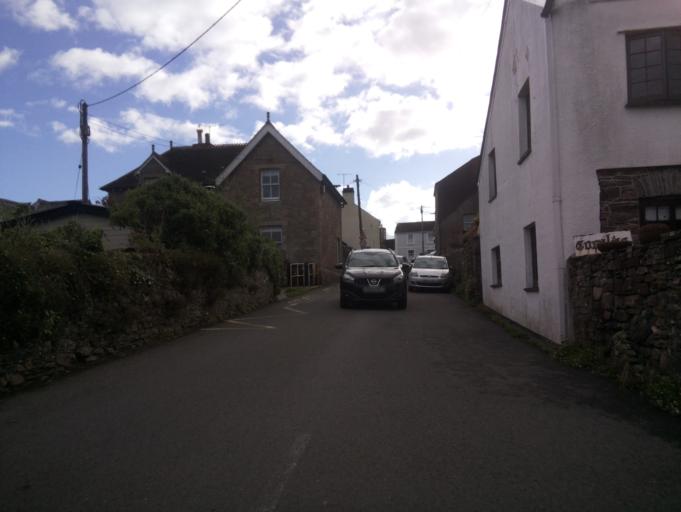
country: GB
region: England
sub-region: Devon
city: Ivybridge
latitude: 50.3621
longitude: -3.9162
